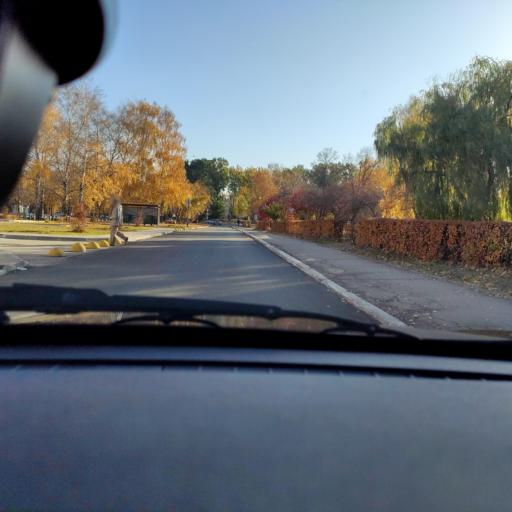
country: RU
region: Samara
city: Tol'yatti
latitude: 53.5230
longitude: 49.3270
